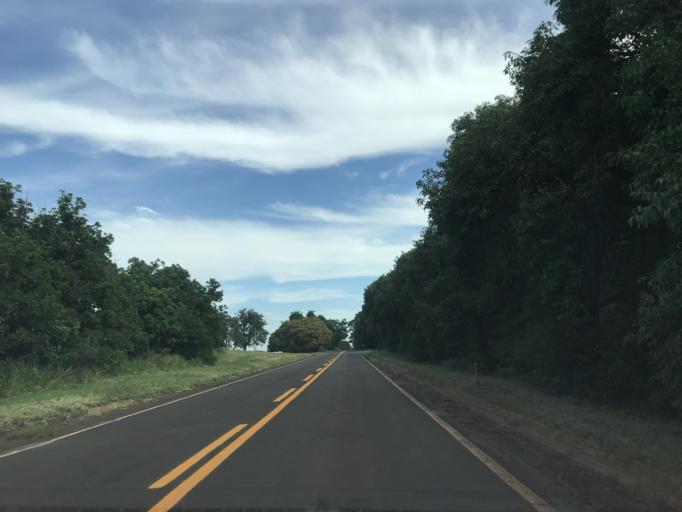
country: BR
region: Parana
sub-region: Terra Rica
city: Terra Rica
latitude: -22.7891
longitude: -52.6548
